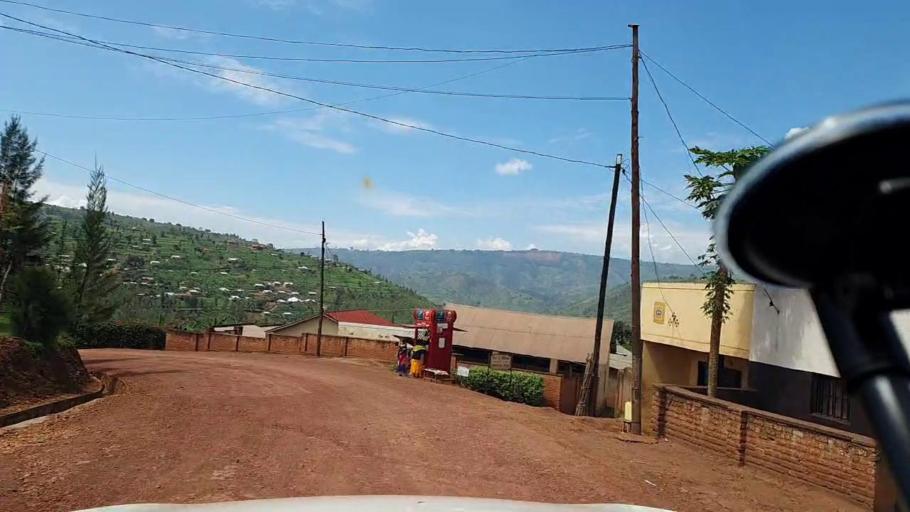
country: RW
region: Kigali
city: Kigali
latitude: -1.8000
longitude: 29.8951
